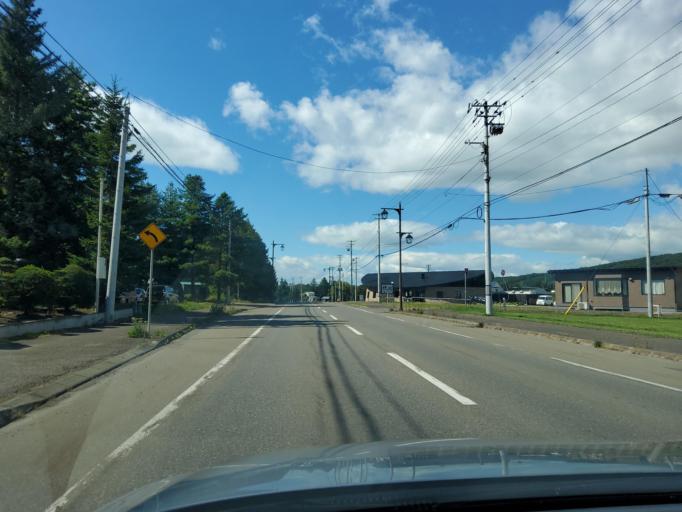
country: JP
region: Hokkaido
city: Obihiro
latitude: 42.9335
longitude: 143.2991
